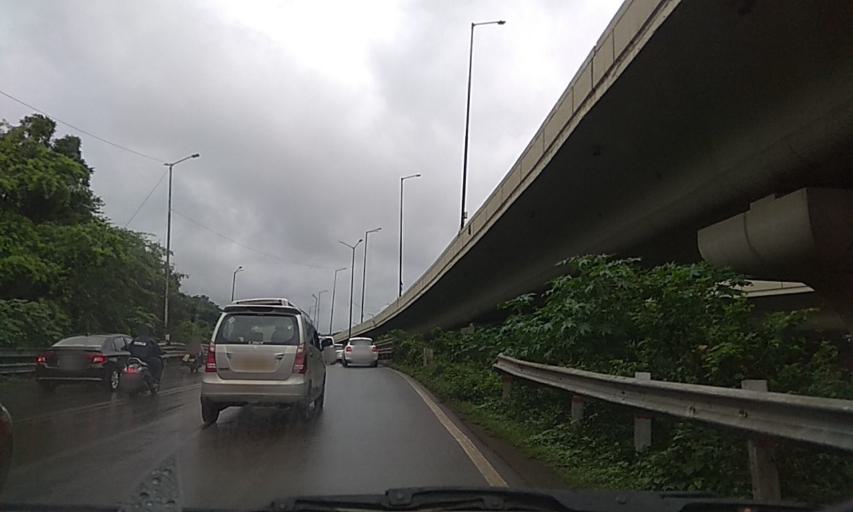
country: IN
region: Maharashtra
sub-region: Pune Division
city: Khadki
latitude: 18.5553
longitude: 73.8618
